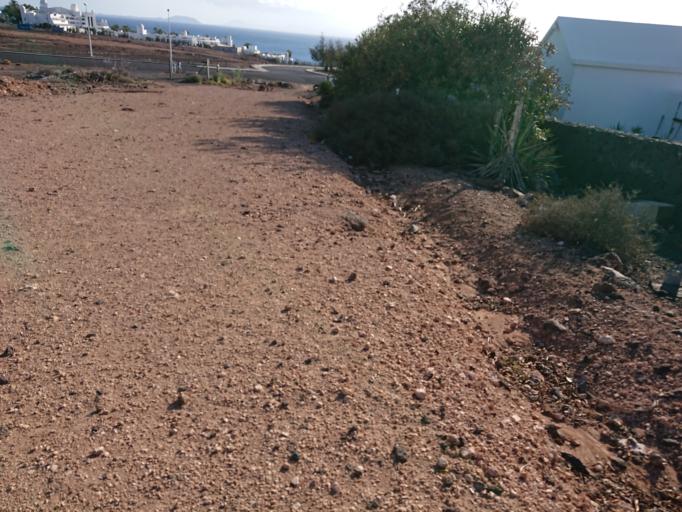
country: ES
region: Canary Islands
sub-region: Provincia de Las Palmas
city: Playa Blanca
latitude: 28.8645
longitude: -13.8460
